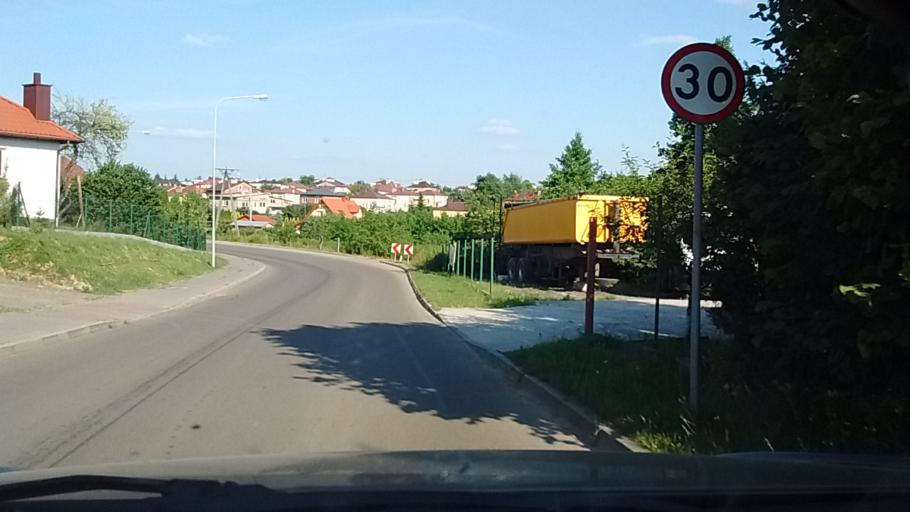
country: PL
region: Subcarpathian Voivodeship
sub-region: Powiat lancucki
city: Lancut
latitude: 50.0577
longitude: 22.2291
